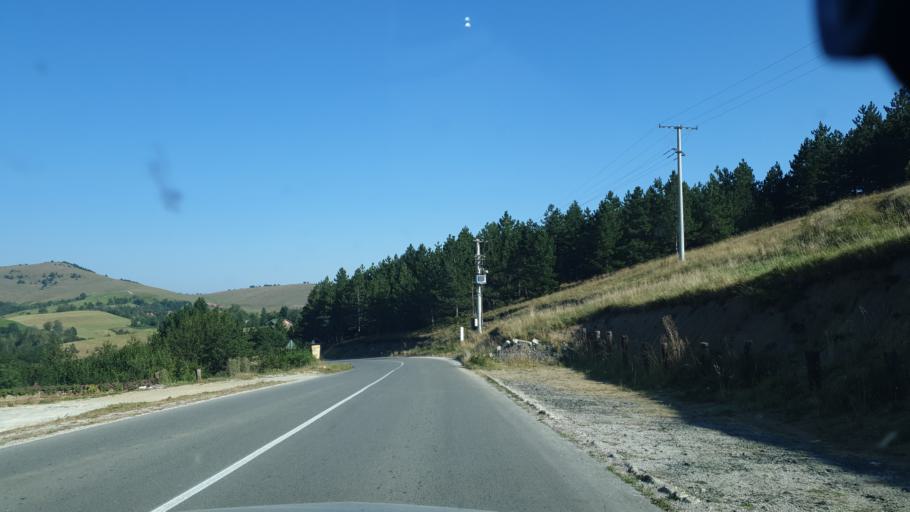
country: RS
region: Central Serbia
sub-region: Zlatiborski Okrug
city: Cajetina
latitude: 43.7165
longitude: 19.7620
